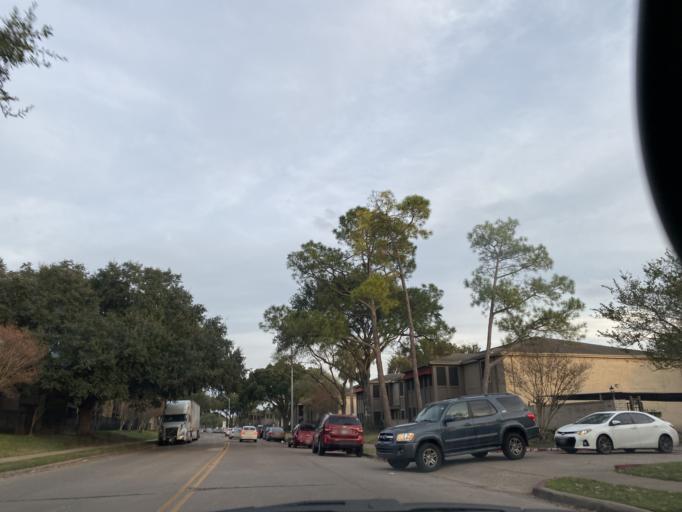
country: US
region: Texas
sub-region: Harris County
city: Bunker Hill Village
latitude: 29.7314
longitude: -95.5637
